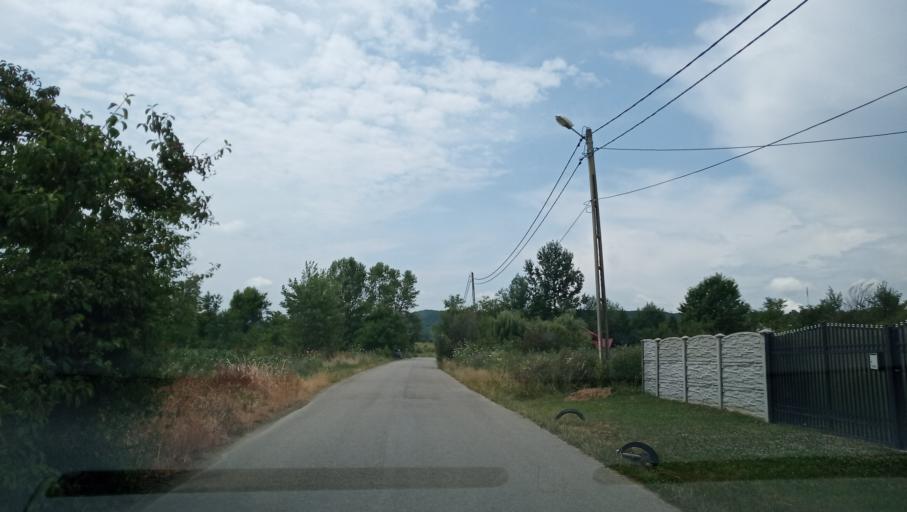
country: RO
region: Gorj
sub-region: Comuna Bumbesti-Jiu
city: Bumbesti-Jiu
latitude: 45.1737
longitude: 23.3605
